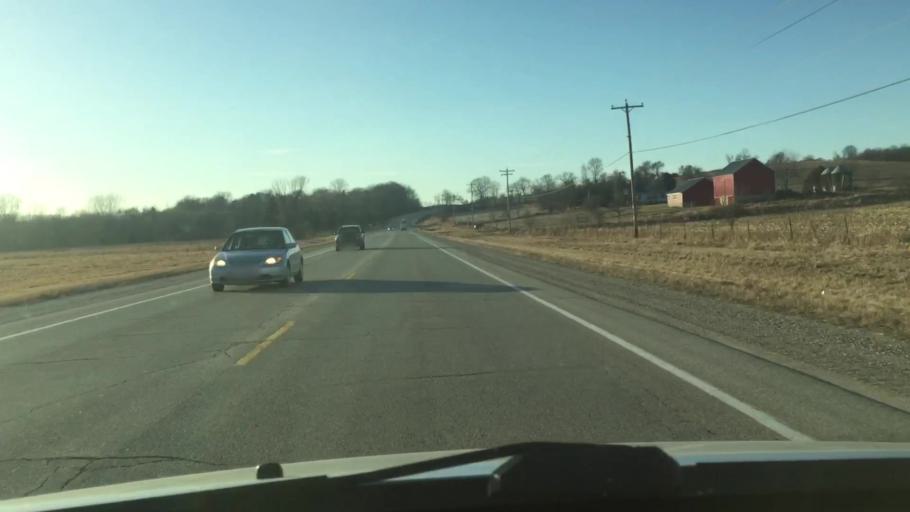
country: US
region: Wisconsin
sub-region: Waukesha County
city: Pewaukee
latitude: 43.1124
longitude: -88.2576
